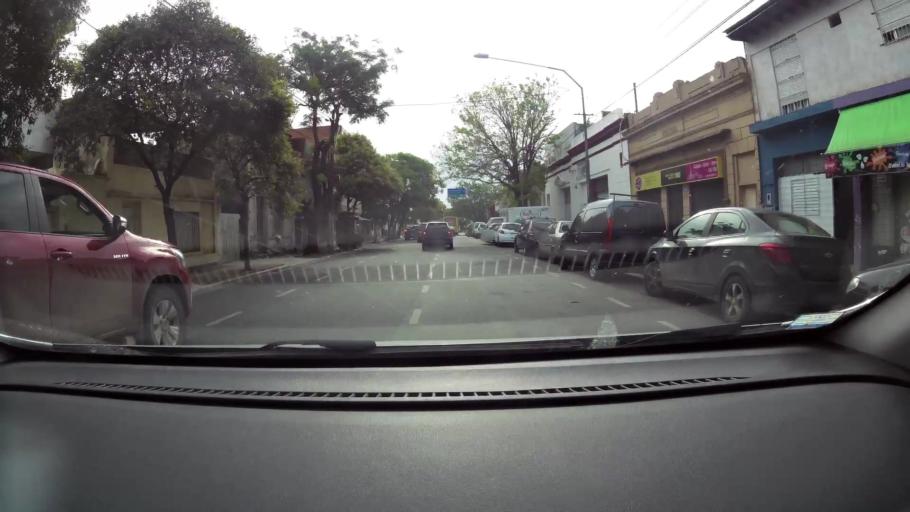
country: AR
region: Santa Fe
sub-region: Departamento de Rosario
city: Rosario
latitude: -32.9247
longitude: -60.6665
